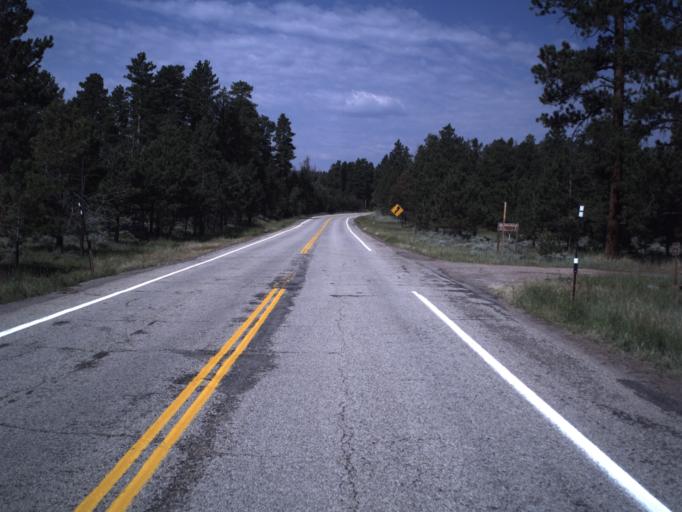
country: US
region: Utah
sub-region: Daggett County
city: Manila
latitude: 40.8518
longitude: -109.6180
